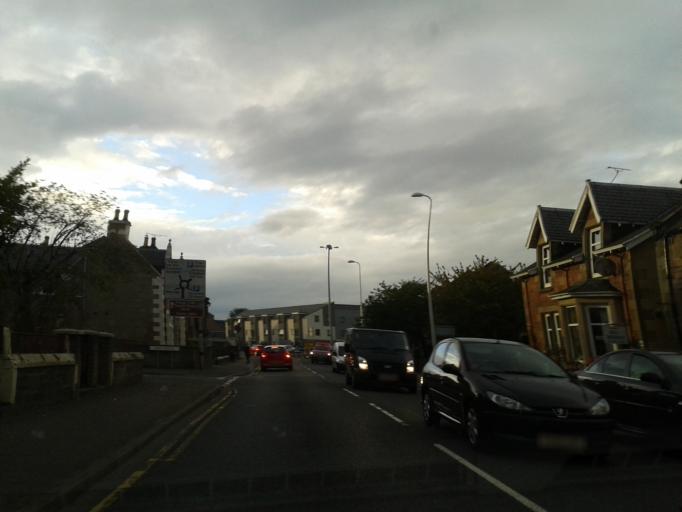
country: GB
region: Scotland
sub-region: Highland
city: Inverness
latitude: 57.4794
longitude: -4.2363
